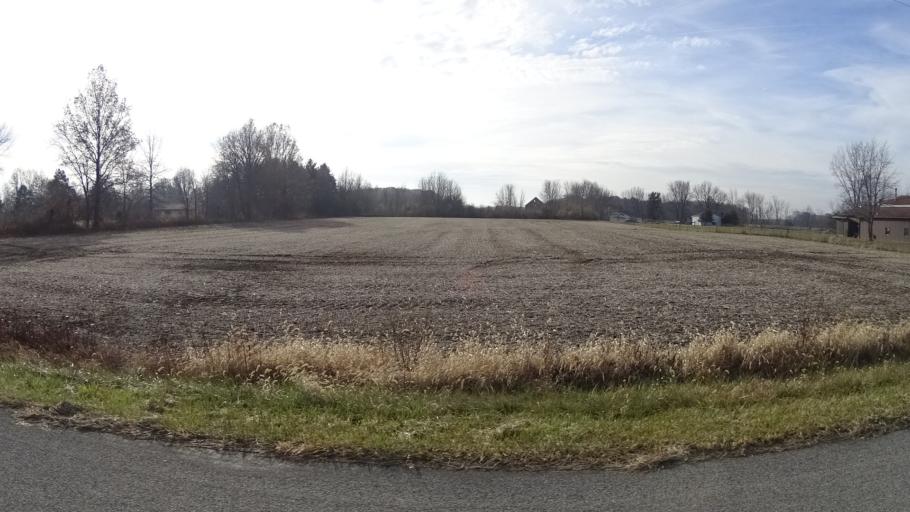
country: US
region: Ohio
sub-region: Lorain County
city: Grafton
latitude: 41.2073
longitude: -81.9781
